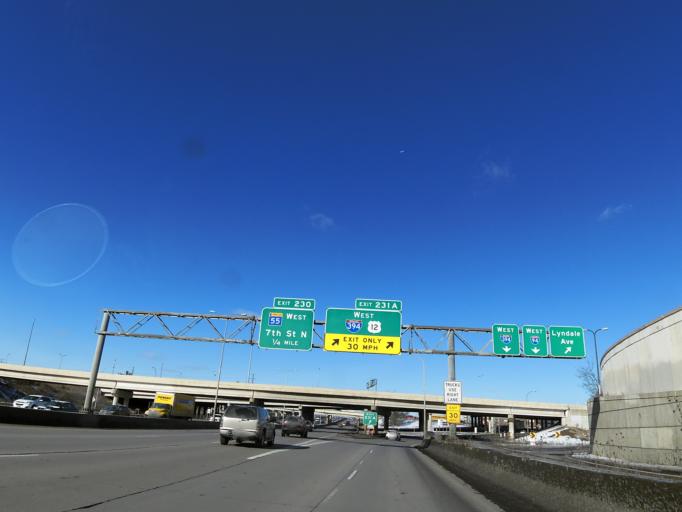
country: US
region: Minnesota
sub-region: Hennepin County
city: Minneapolis
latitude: 44.9735
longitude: -93.2873
